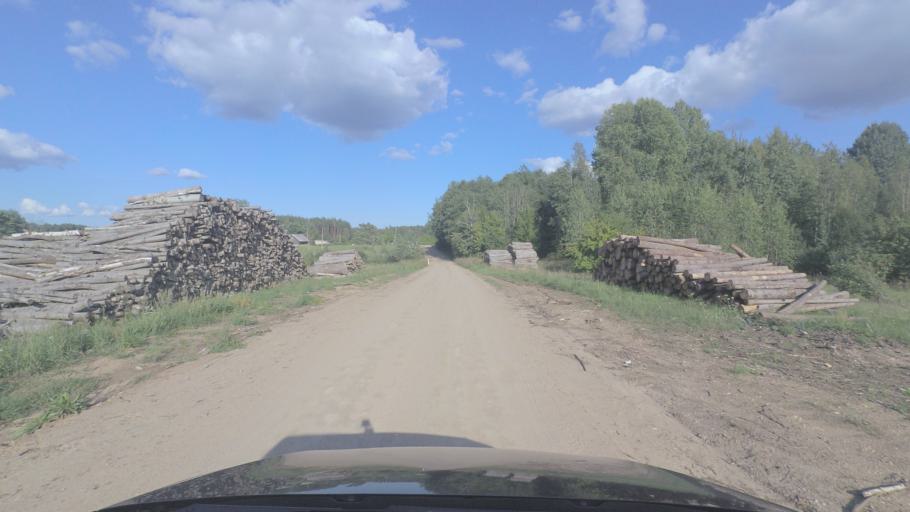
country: LT
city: Pabrade
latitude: 55.1402
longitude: 25.7330
